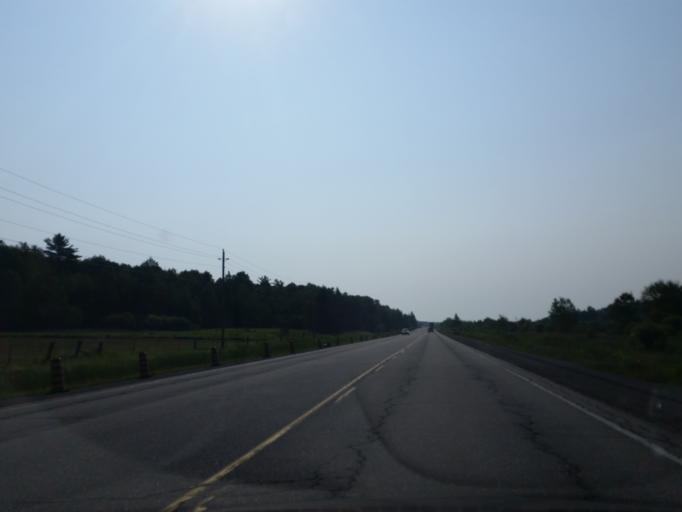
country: CA
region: Ontario
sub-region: Nipissing District
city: North Bay
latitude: 46.4281
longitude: -80.2078
